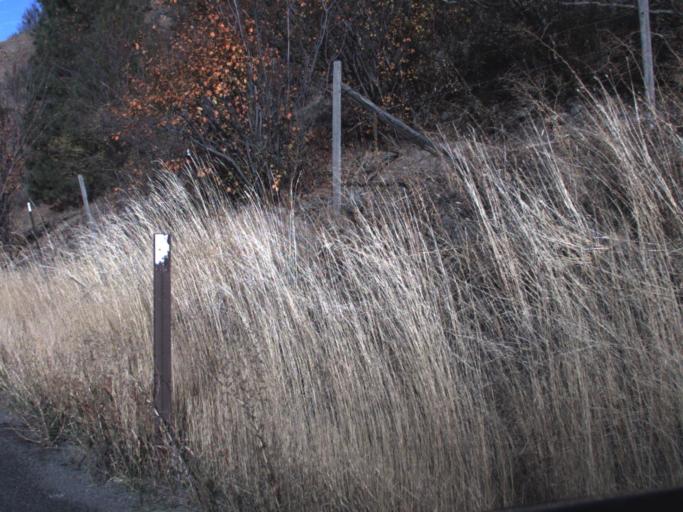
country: US
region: Washington
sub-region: Lincoln County
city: Davenport
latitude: 48.1225
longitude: -118.2090
